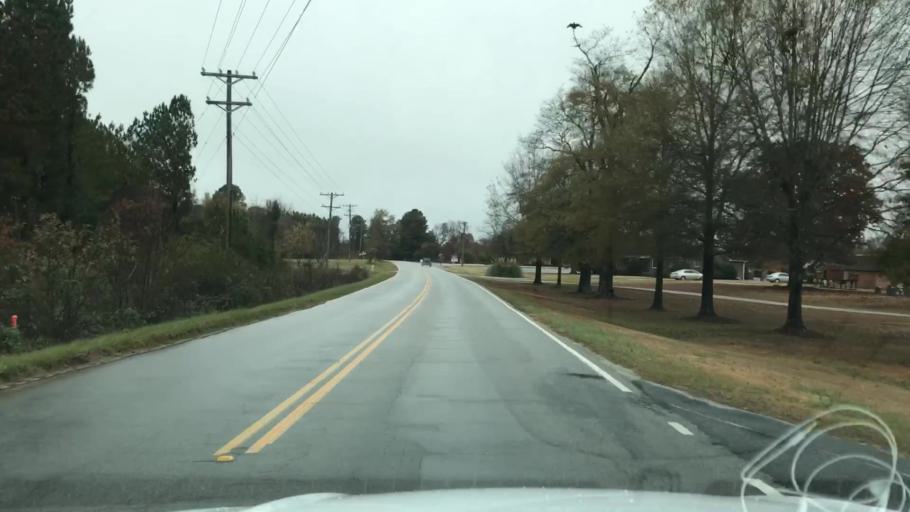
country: US
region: South Carolina
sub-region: Spartanburg County
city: Roebuck
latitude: 34.8022
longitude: -81.9166
